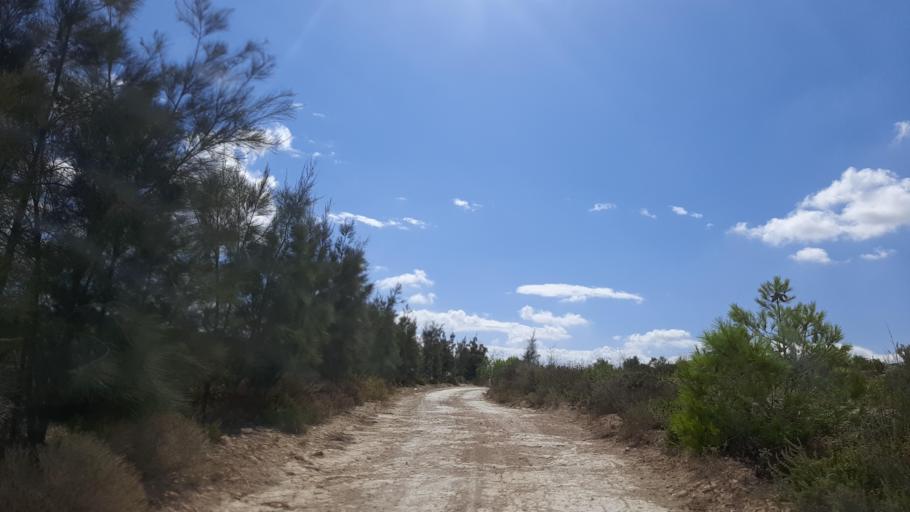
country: TN
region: Zaghwan
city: Zaghouan
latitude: 36.4971
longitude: 10.1723
